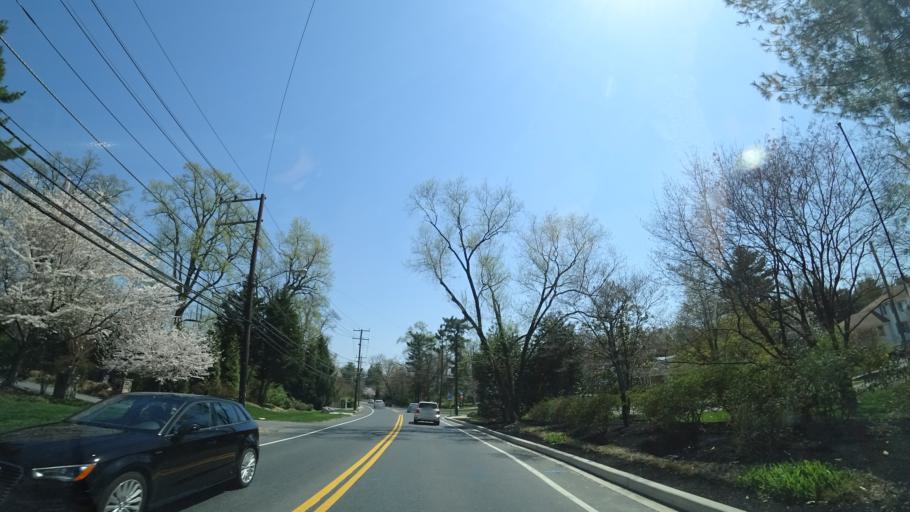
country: US
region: Maryland
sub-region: Montgomery County
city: Bethesda
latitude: 38.9786
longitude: -77.1100
